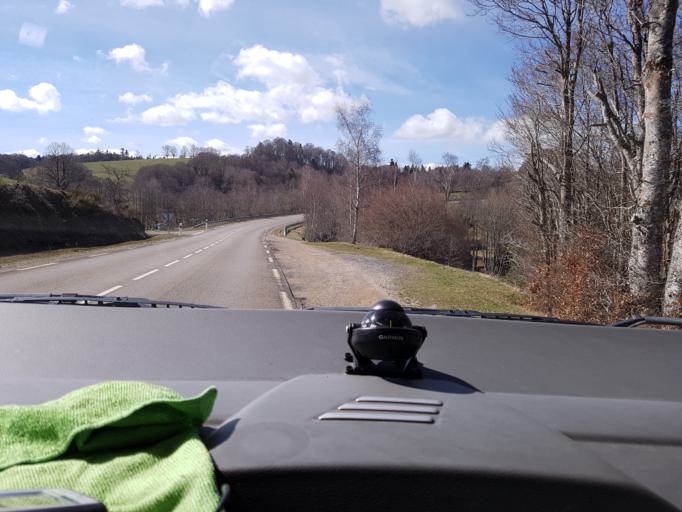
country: FR
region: Midi-Pyrenees
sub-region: Departement de l'Aveyron
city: Laguiole
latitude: 44.7797
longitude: 2.9048
